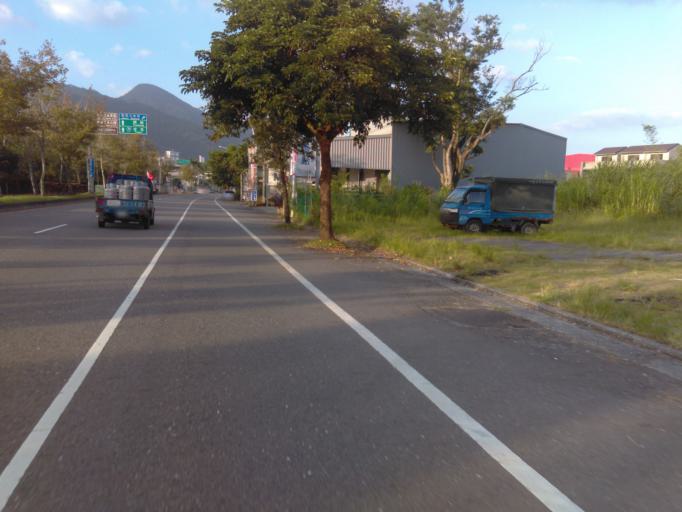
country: TW
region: Taiwan
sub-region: Yilan
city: Yilan
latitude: 24.8140
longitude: 121.7676
